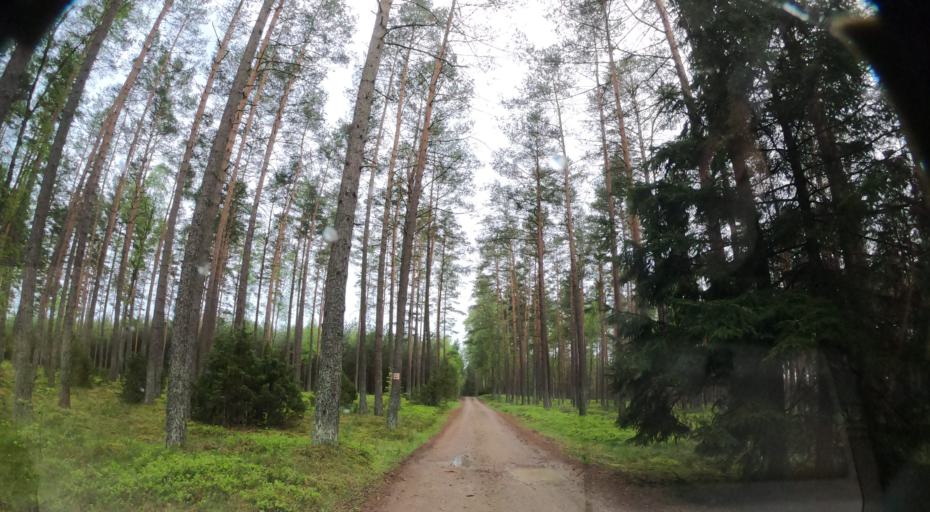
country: PL
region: West Pomeranian Voivodeship
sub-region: Powiat koszalinski
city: Bobolice
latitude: 54.0655
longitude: 16.4354
